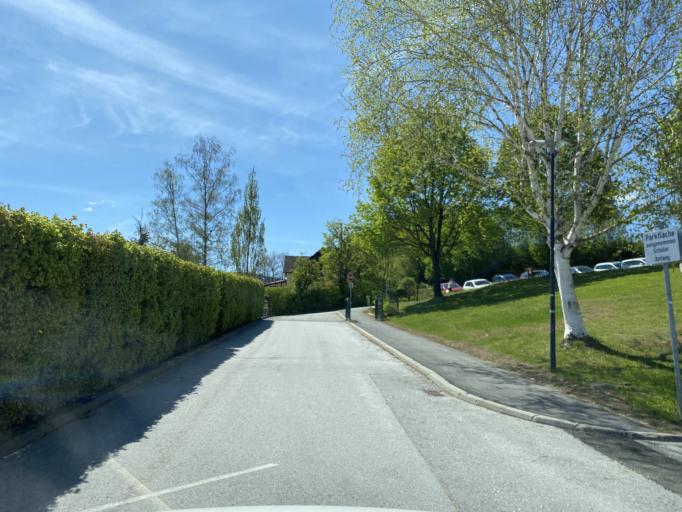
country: AT
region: Styria
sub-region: Politischer Bezirk Weiz
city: Birkfeld
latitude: 47.3525
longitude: 15.6913
